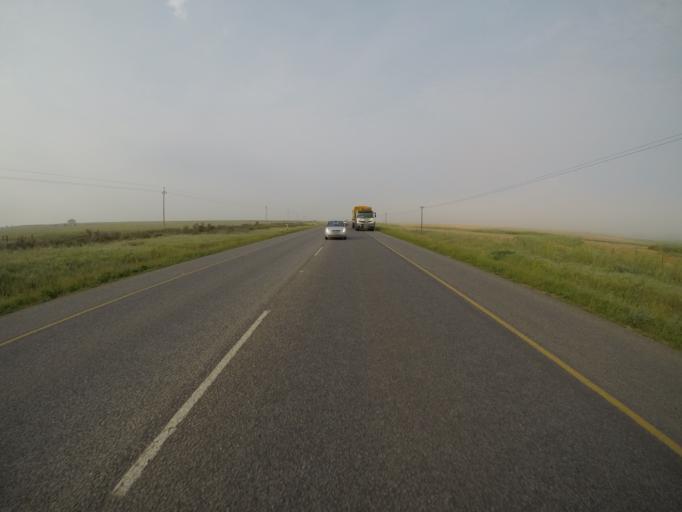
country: ZA
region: Western Cape
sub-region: West Coast District Municipality
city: Malmesbury
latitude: -33.6512
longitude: 18.7103
